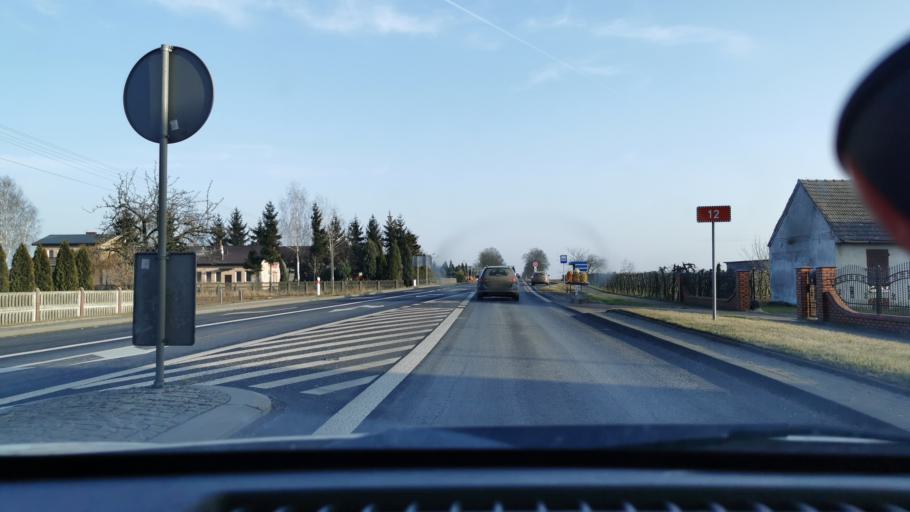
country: PL
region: Lodz Voivodeship
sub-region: Powiat sieradzki
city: Wroblew
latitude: 51.6301
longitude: 18.5516
